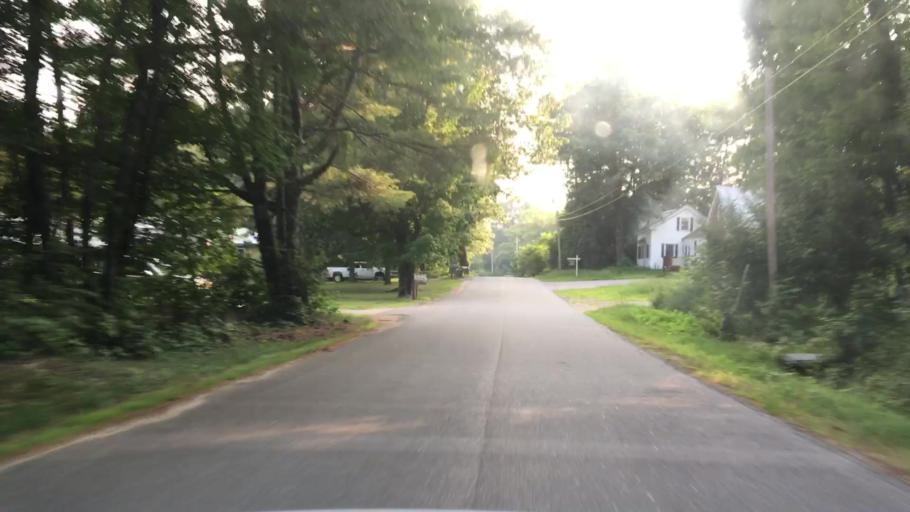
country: US
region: Maine
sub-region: Oxford County
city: Bethel
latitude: 44.4108
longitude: -70.8658
